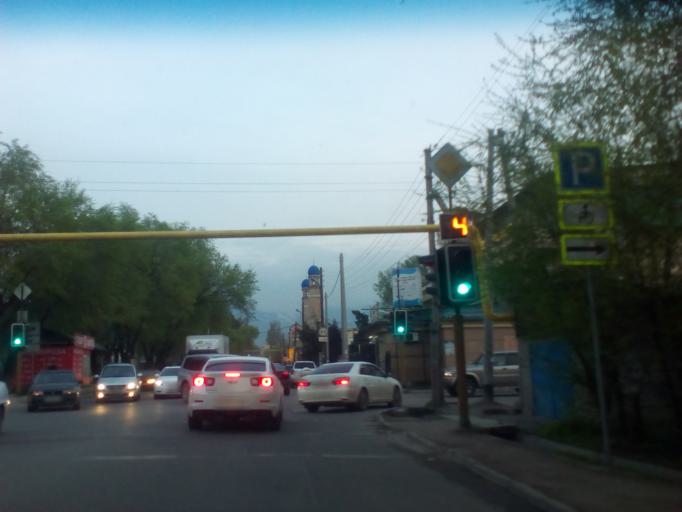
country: KZ
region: Almaty Qalasy
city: Almaty
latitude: 43.2262
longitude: 76.8282
